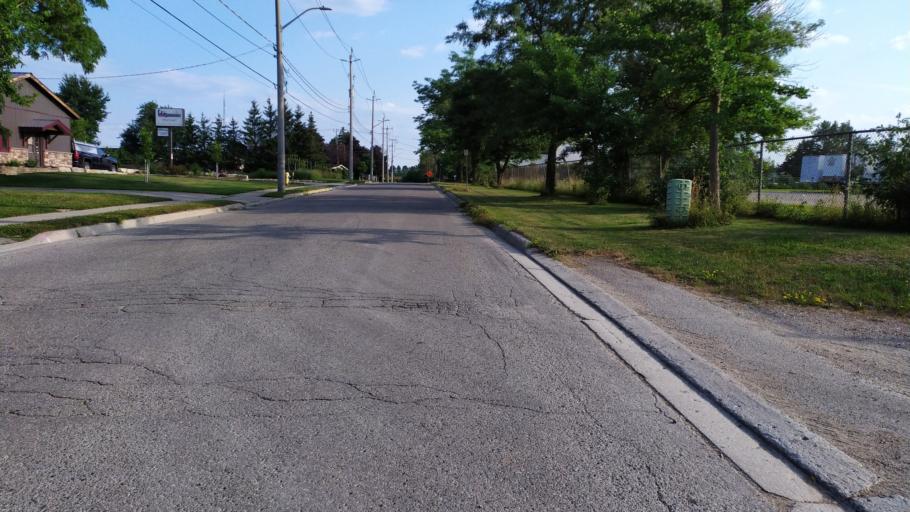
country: CA
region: Ontario
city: Stratford
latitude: 43.3669
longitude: -80.9668
